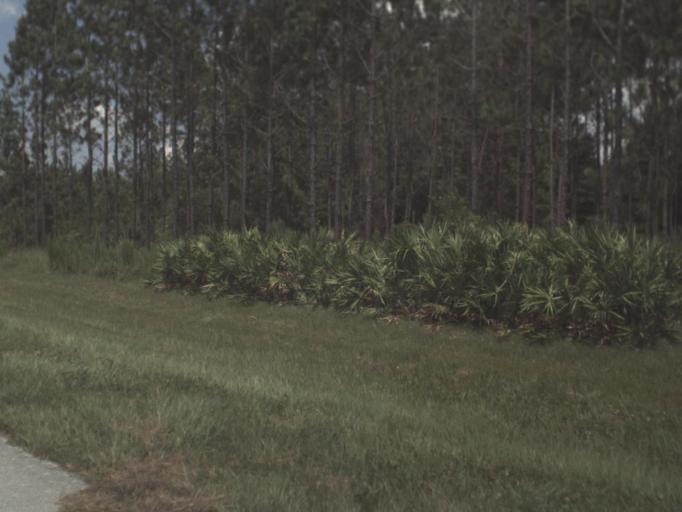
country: US
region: Florida
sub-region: Baker County
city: Macclenny
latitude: 30.2067
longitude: -82.1556
